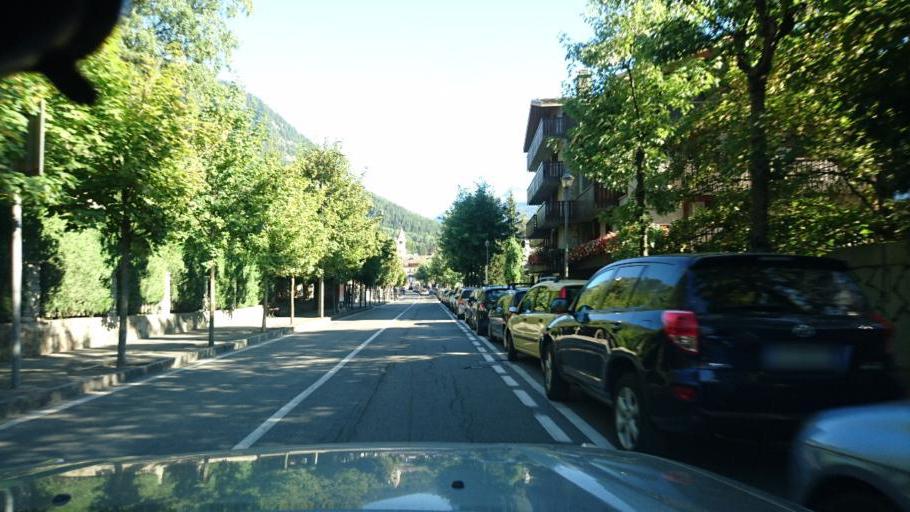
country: IT
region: Aosta Valley
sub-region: Valle d'Aosta
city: Courmayeur
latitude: 45.7946
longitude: 6.9701
